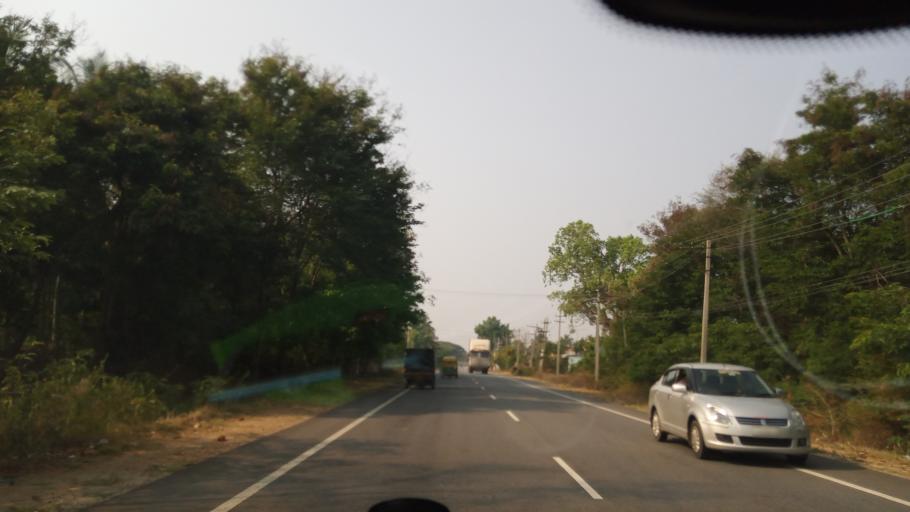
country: IN
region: Karnataka
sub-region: Mandya
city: Belluru
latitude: 12.9314
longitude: 76.7497
